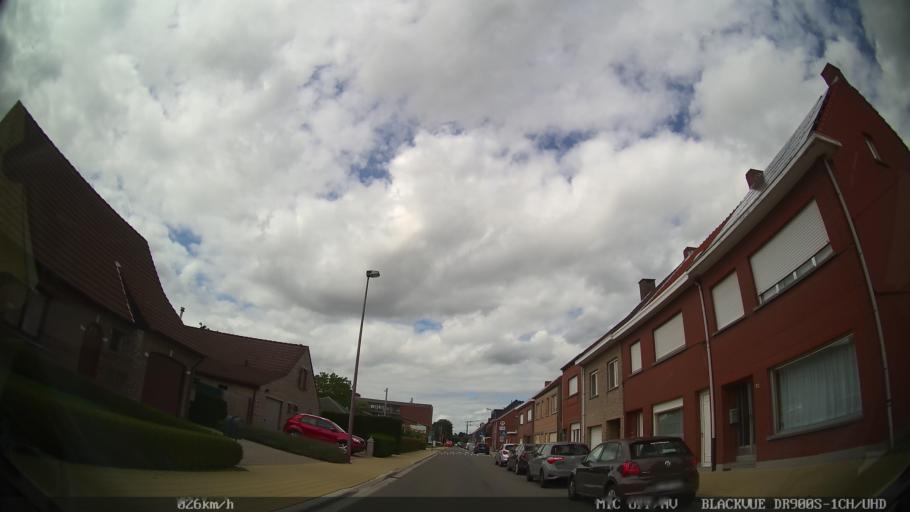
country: BE
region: Flanders
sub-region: Provincie Antwerpen
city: Stabroek
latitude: 51.3310
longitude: 4.3745
